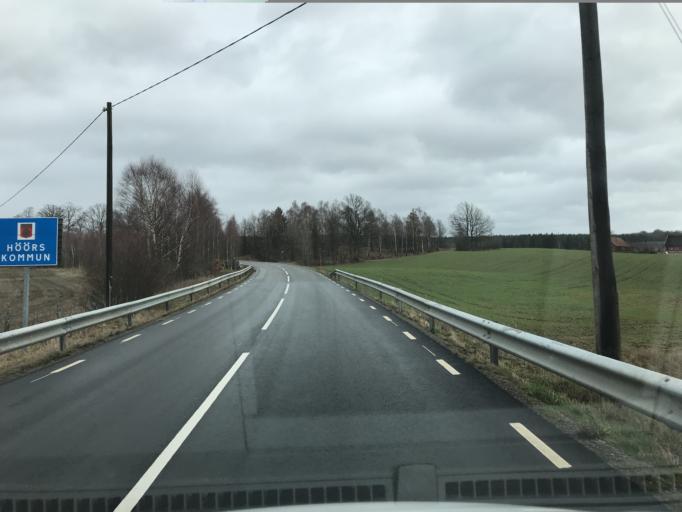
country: SE
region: Skane
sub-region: Perstorps Kommun
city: Perstorp
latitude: 56.0220
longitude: 13.4440
